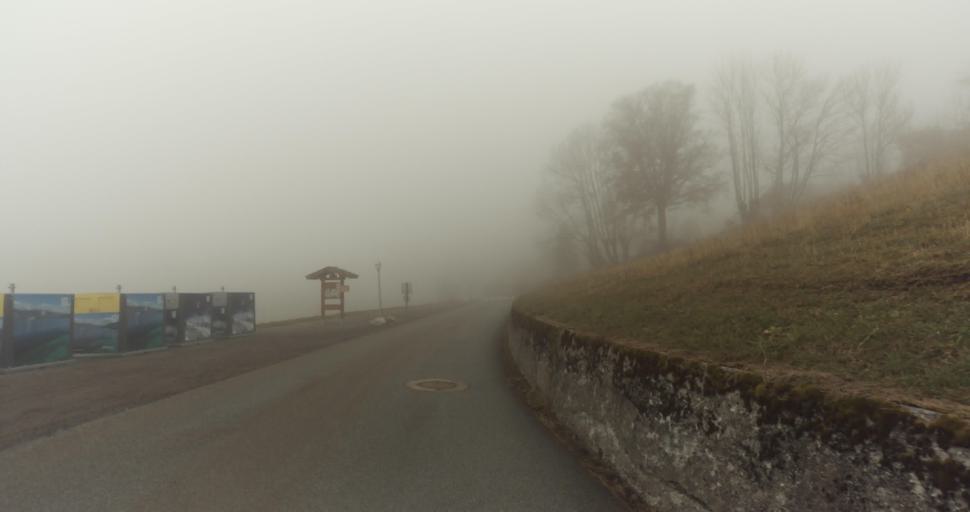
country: FR
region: Rhone-Alpes
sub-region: Departement de la Haute-Savoie
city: Doussard
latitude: 45.8035
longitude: 6.2634
